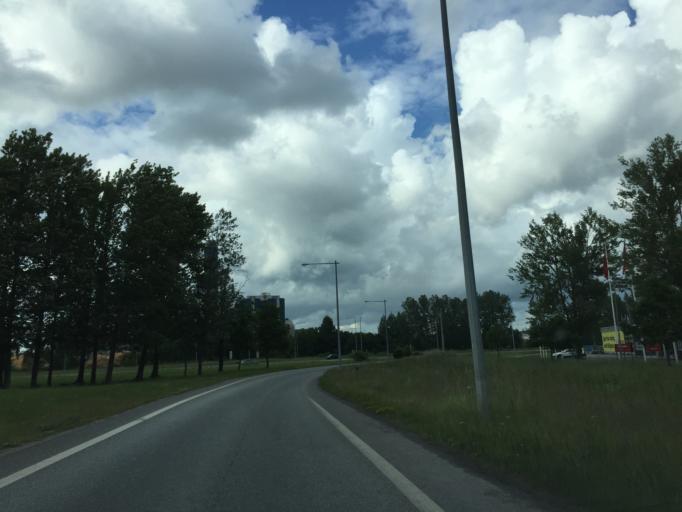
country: SE
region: OErebro
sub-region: Orebro Kommun
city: Orebro
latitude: 59.2615
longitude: 15.1775
